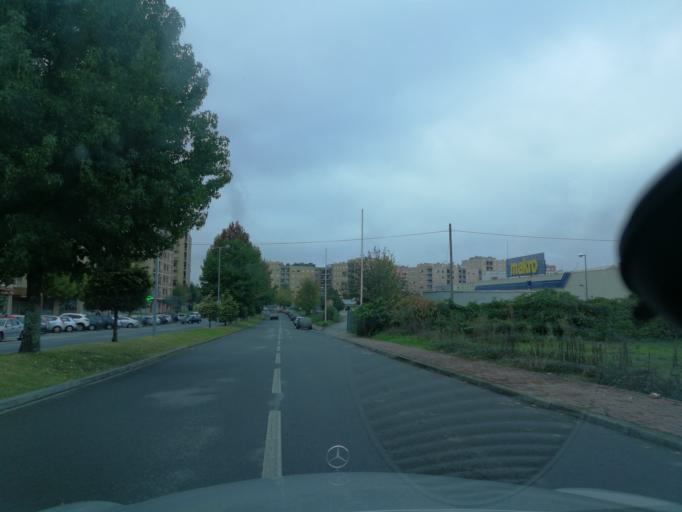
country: PT
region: Braga
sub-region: Braga
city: Braga
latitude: 41.5481
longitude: -8.3999
